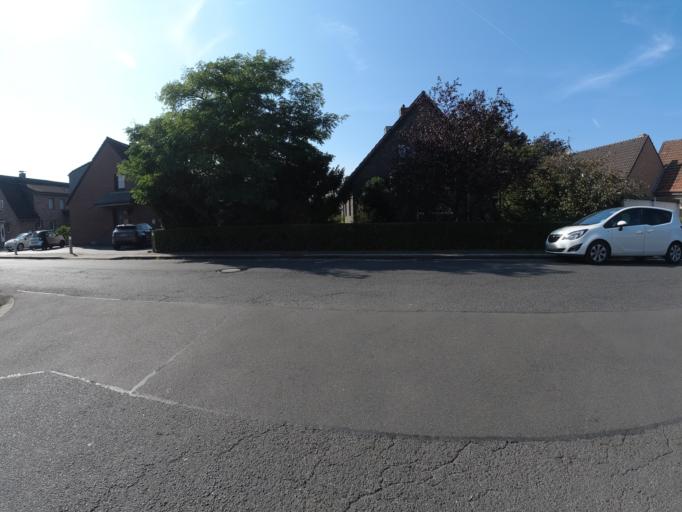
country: DE
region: North Rhine-Westphalia
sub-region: Regierungsbezirk Dusseldorf
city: Moers
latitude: 51.4597
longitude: 6.6626
